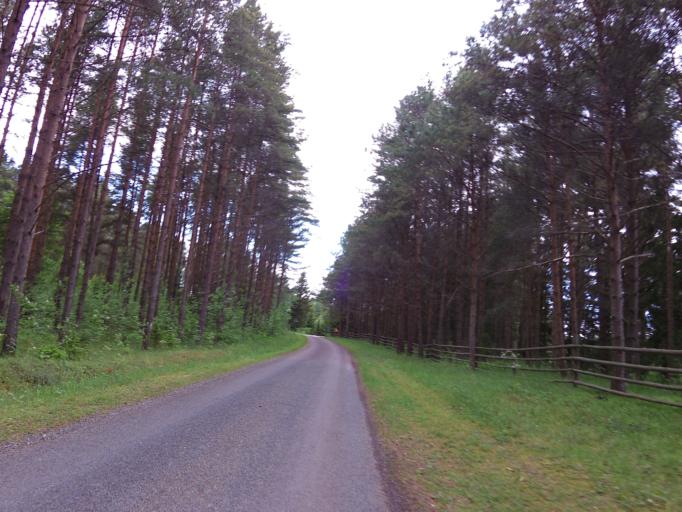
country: EE
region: Harju
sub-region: Paldiski linn
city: Paldiski
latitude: 59.2536
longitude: 23.7513
